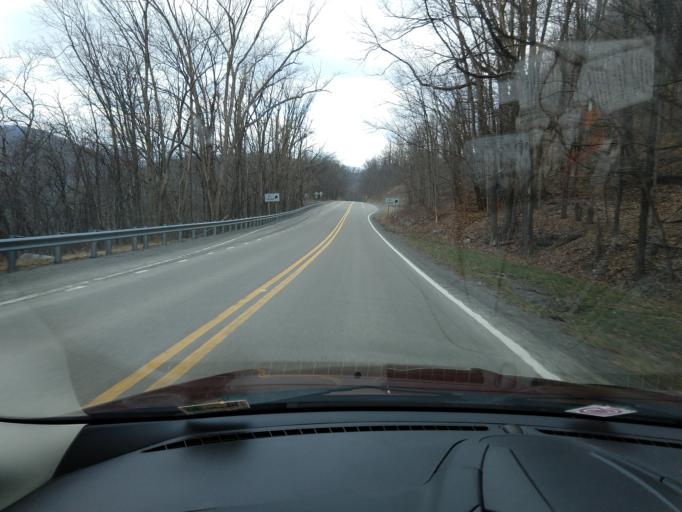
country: US
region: West Virginia
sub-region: Randolph County
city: Elkins
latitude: 38.6555
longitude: -79.9208
